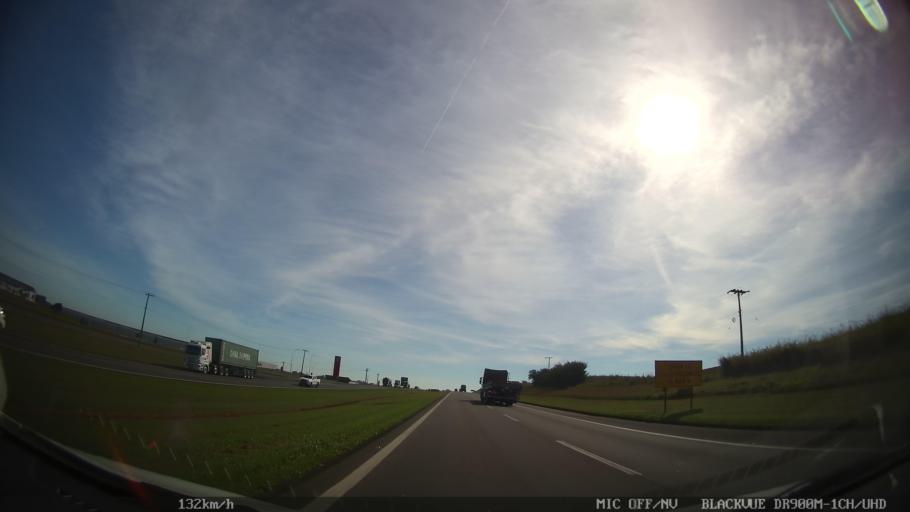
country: BR
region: Sao Paulo
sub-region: Cordeiropolis
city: Cordeiropolis
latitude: -22.4952
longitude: -47.3993
